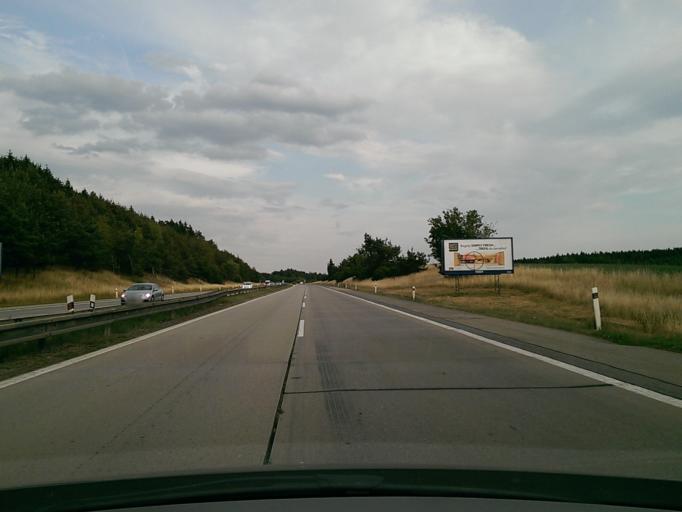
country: CZ
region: Vysocina
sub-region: Okres Zd'ar nad Sazavou
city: Velke Mezirici
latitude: 49.3397
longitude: 16.0541
